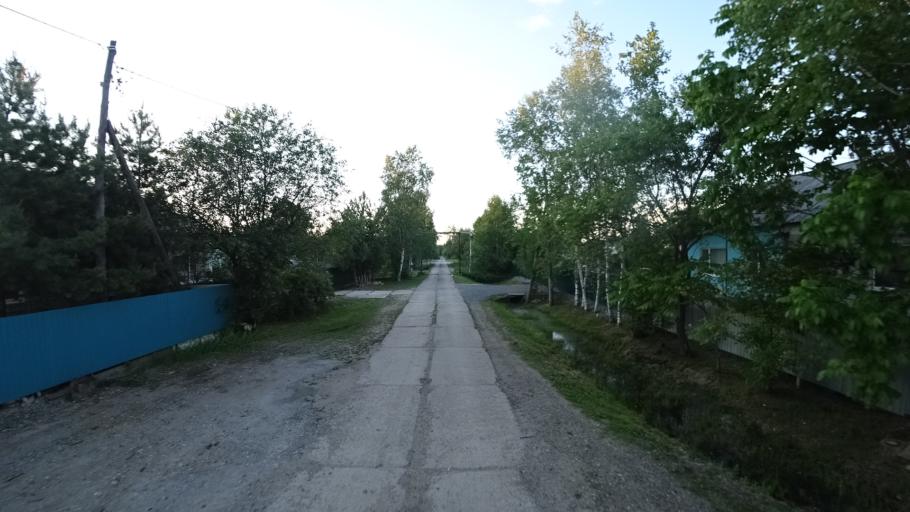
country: RU
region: Khabarovsk Krai
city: Khor
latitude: 47.8452
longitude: 134.9528
